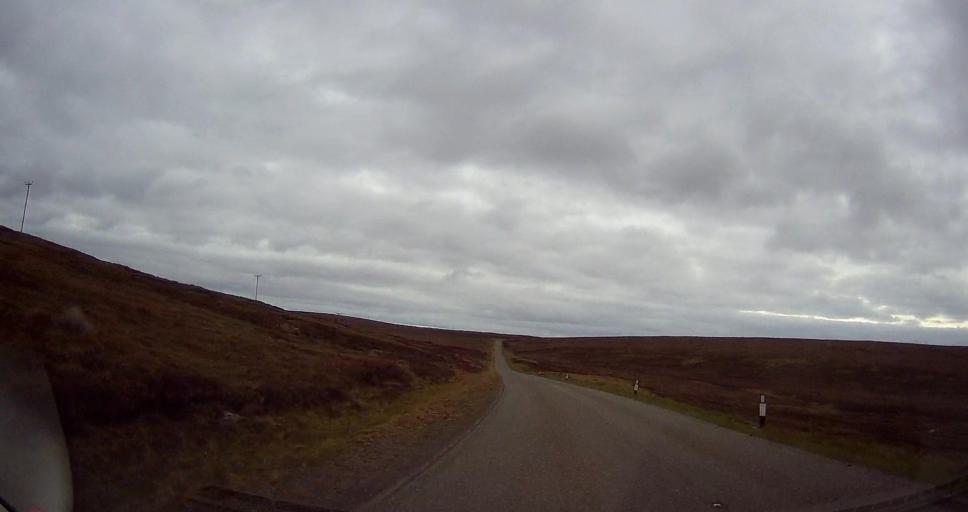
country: GB
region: Scotland
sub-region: Shetland Islands
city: Shetland
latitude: 60.6693
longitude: -1.0104
